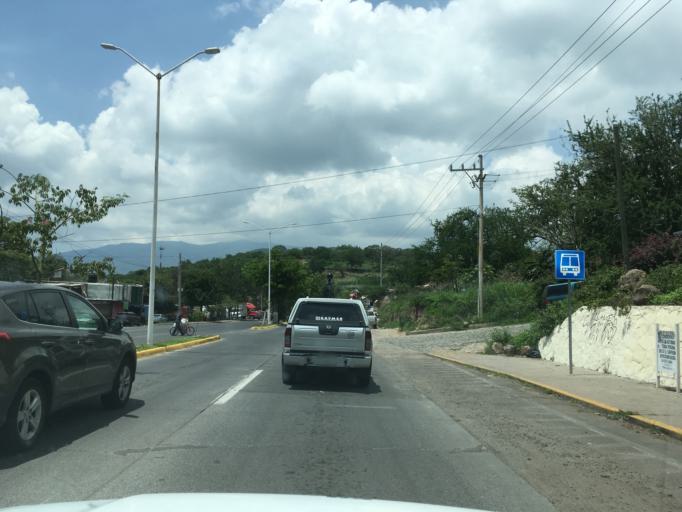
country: MX
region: Jalisco
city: Tlajomulco de Zuniga
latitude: 20.4705
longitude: -103.4522
